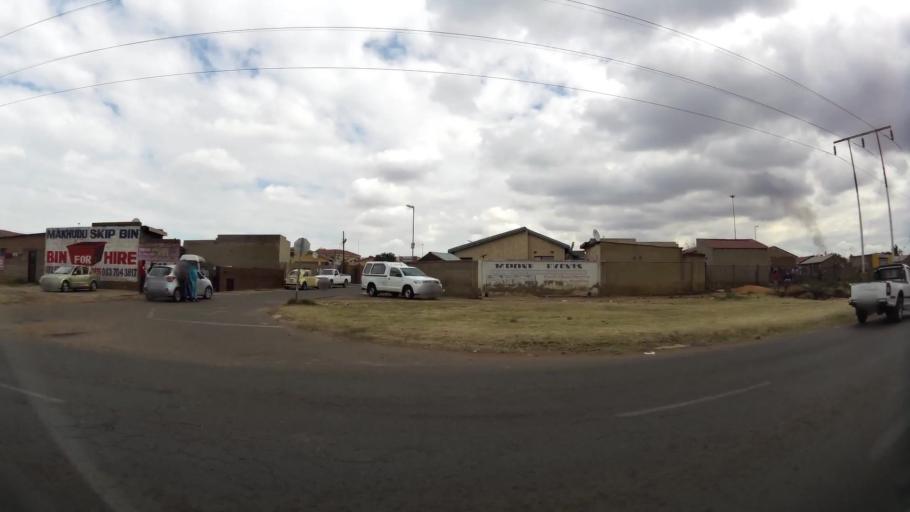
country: ZA
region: Gauteng
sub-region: City of Johannesburg Metropolitan Municipality
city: Soweto
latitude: -26.2691
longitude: 27.8606
